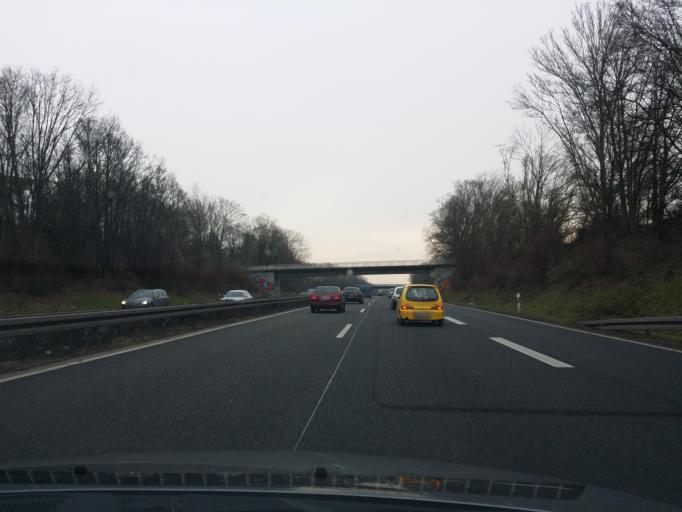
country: DE
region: Hesse
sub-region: Regierungsbezirk Darmstadt
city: Hochheim am Main
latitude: 50.0141
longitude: 8.3393
